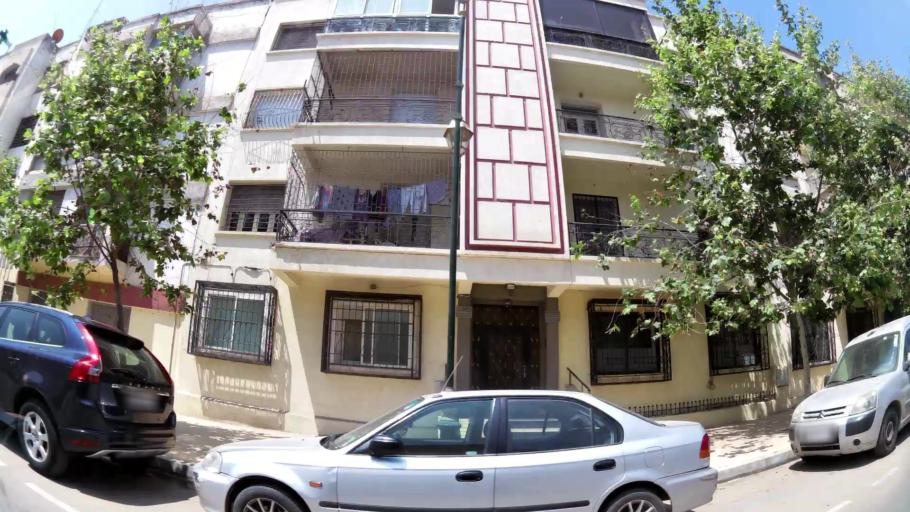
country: MA
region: Rabat-Sale-Zemmour-Zaer
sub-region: Rabat
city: Rabat
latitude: 34.0253
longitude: -6.8416
